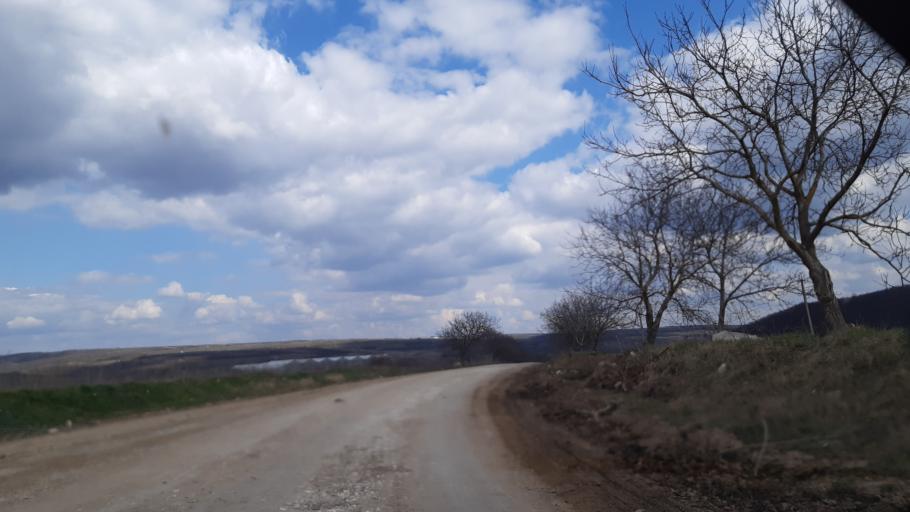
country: MD
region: Laloveni
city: Ialoveni
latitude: 46.8893
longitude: 28.7140
